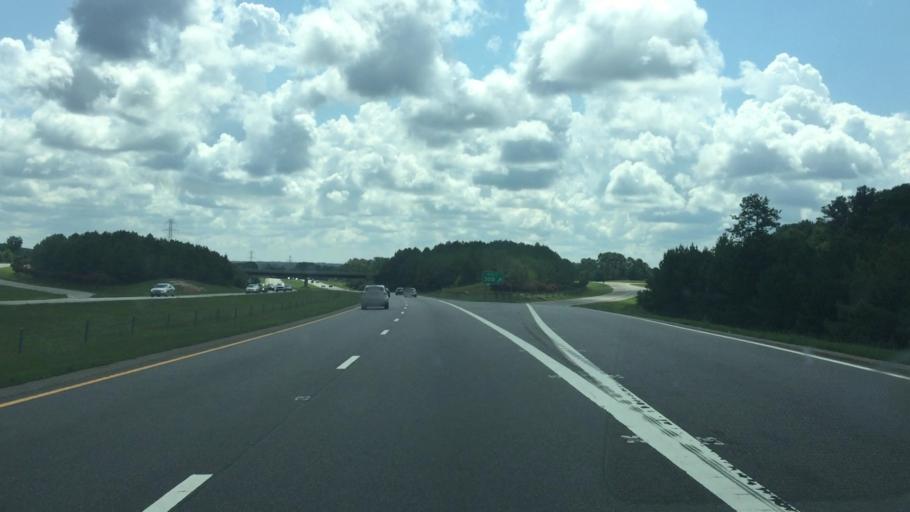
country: US
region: North Carolina
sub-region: Richmond County
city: Cordova
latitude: 34.9334
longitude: -79.8357
